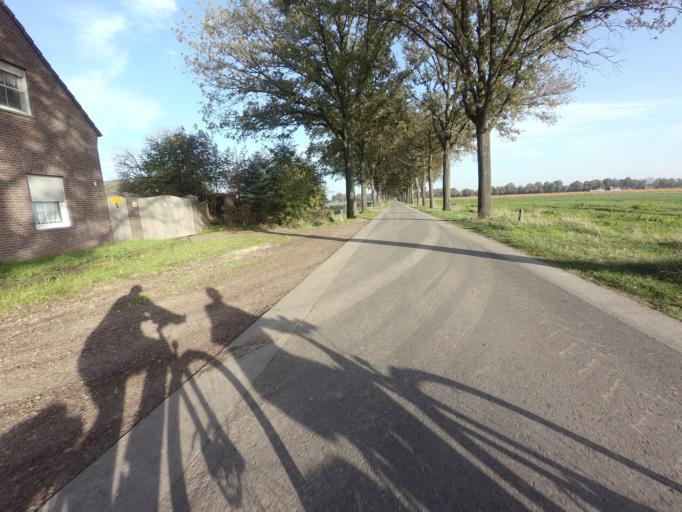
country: NL
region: Limburg
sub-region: Gemeente Roerdalen
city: Montfort
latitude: 51.1110
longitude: 5.9609
